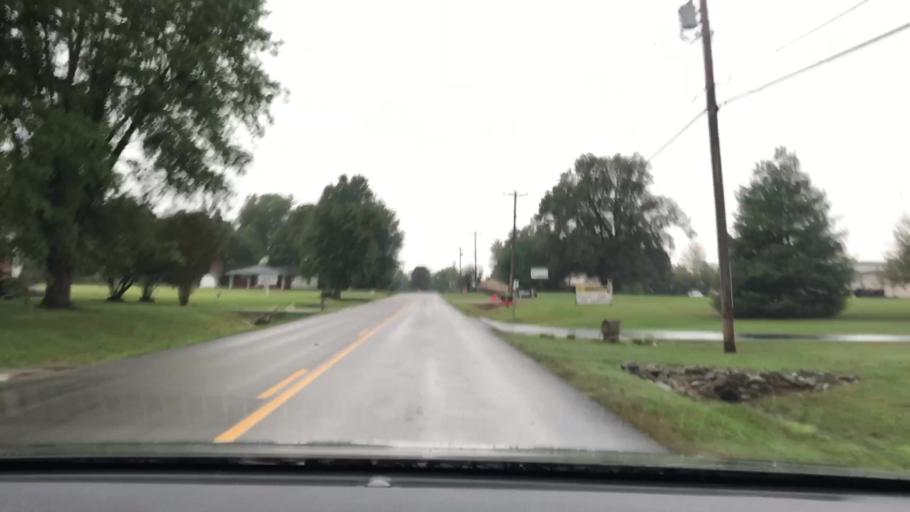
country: US
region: Kentucky
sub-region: Hopkins County
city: Madisonville
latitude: 37.3499
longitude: -87.4000
